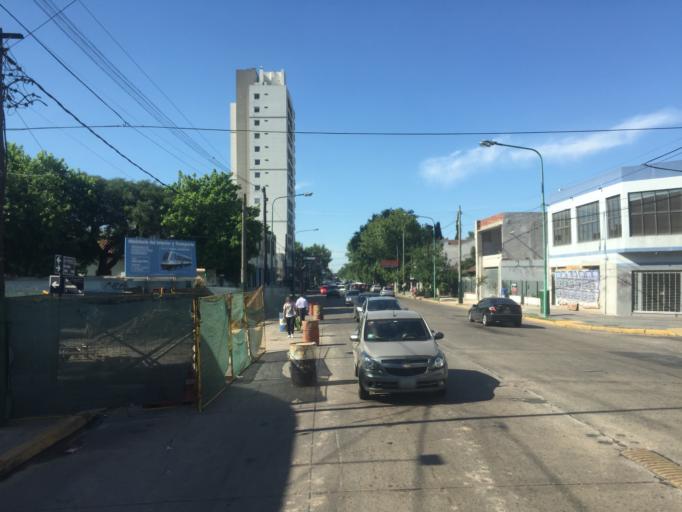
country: AR
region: Buenos Aires
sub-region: Partido de Lomas de Zamora
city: Lomas de Zamora
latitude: -34.7590
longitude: -58.3960
